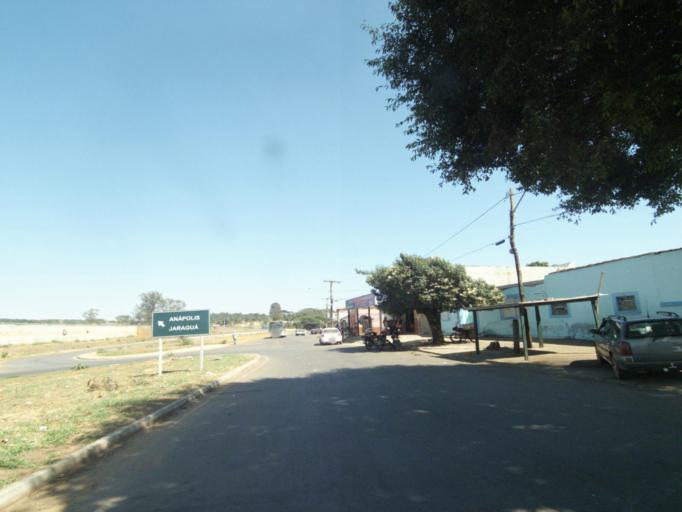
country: BR
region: Goias
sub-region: Anapolis
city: Anapolis
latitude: -16.1901
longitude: -49.0348
